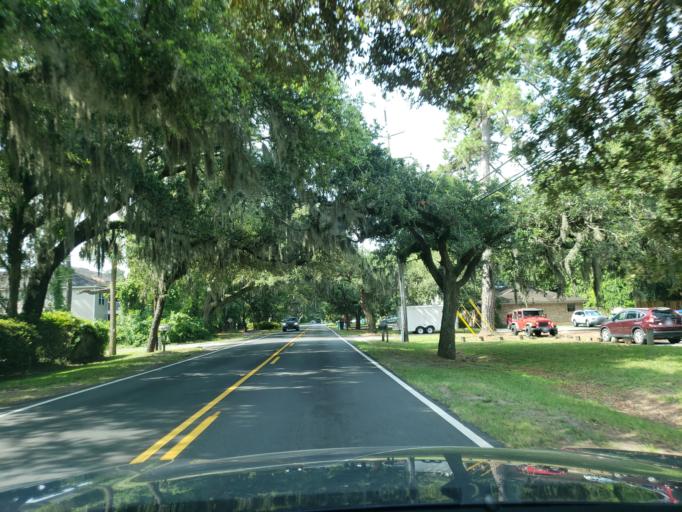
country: US
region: Georgia
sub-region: Chatham County
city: Wilmington Island
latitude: 32.0298
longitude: -80.9647
